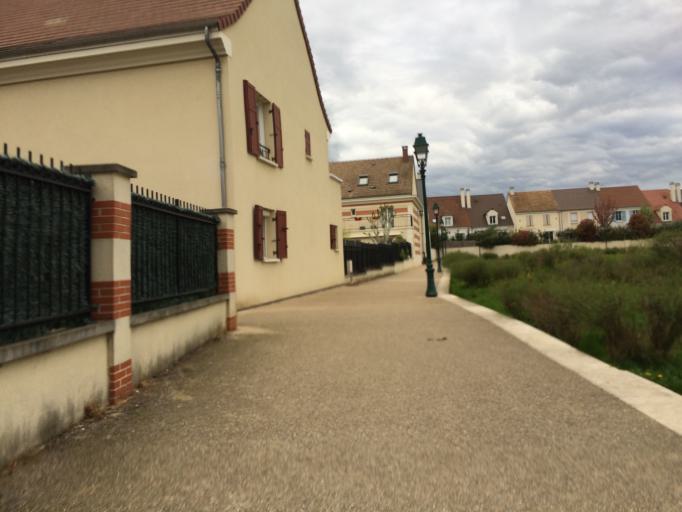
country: FR
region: Ile-de-France
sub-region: Departement de l'Essonne
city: Wissous
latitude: 48.7391
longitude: 2.3284
